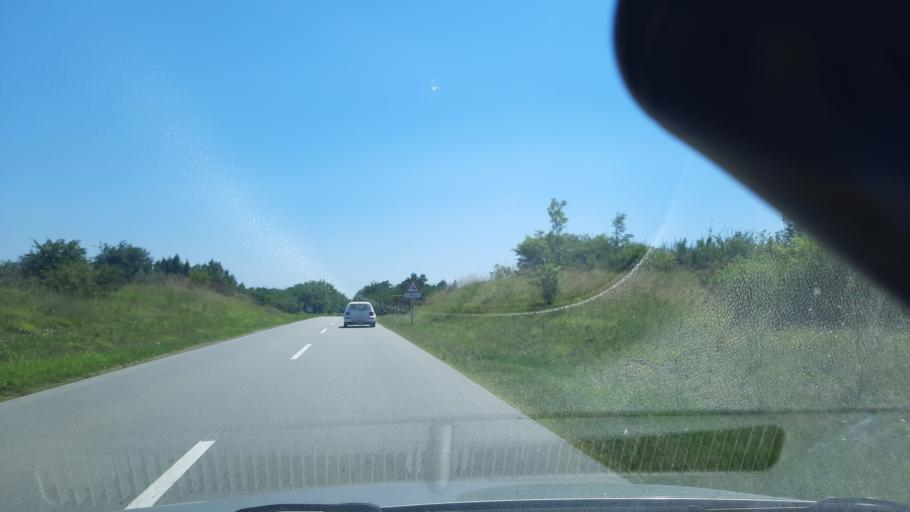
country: RO
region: Caras-Severin
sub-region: Comuna Socol
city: Socol
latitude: 44.8061
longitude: 21.2285
